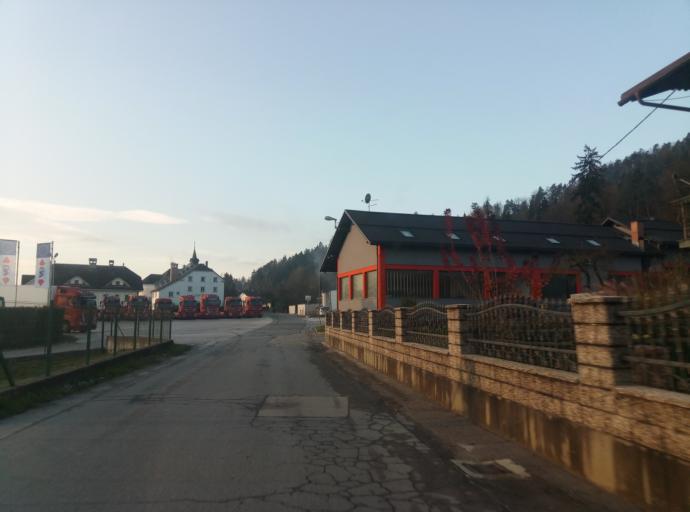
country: SI
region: Vodice
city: Vodice
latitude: 46.1730
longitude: 14.4826
